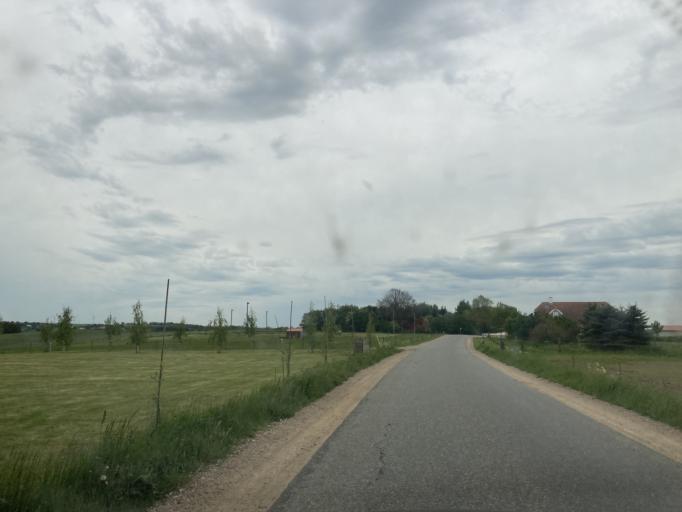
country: DK
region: Zealand
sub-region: Roskilde Kommune
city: Svogerslev
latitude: 55.6485
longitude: 11.9884
